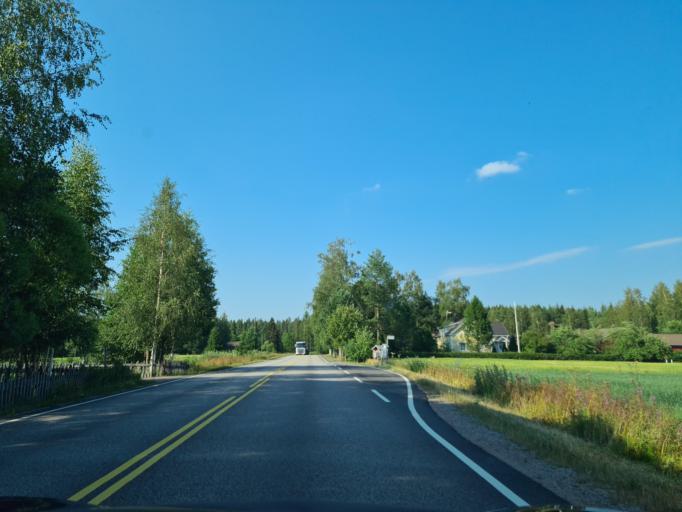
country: FI
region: Satakunta
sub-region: Pohjois-Satakunta
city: Karvia
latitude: 62.1994
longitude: 22.5967
